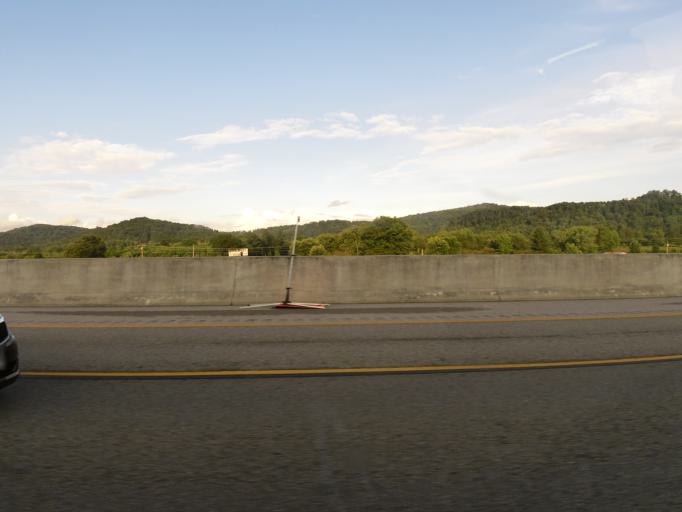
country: US
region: Kentucky
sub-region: Madison County
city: Berea
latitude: 37.4824
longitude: -84.3321
